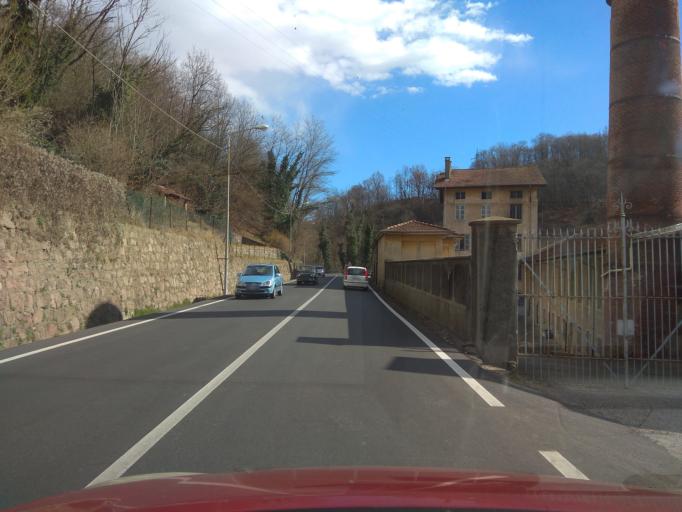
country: IT
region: Piedmont
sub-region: Provincia di Biella
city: Fontanella-Ozino
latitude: 45.6122
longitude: 8.1673
